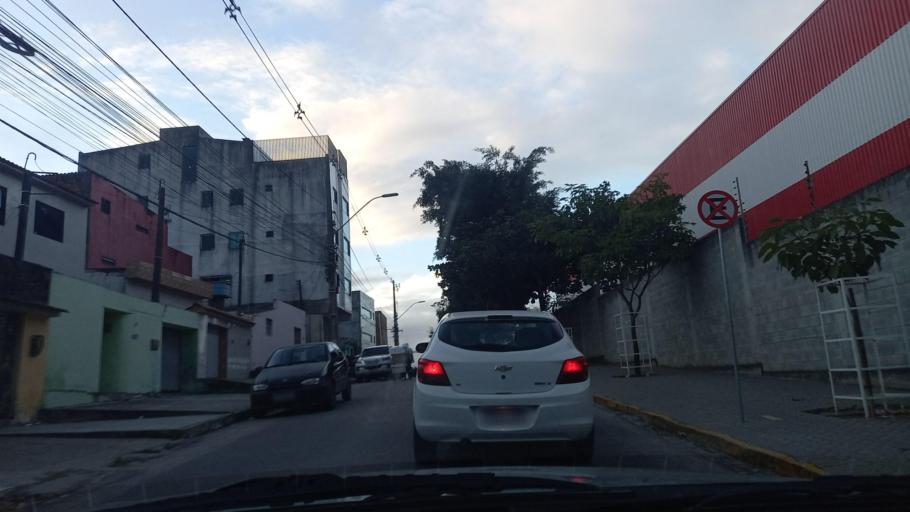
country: BR
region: Pernambuco
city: Garanhuns
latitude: -8.8825
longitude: -36.4662
